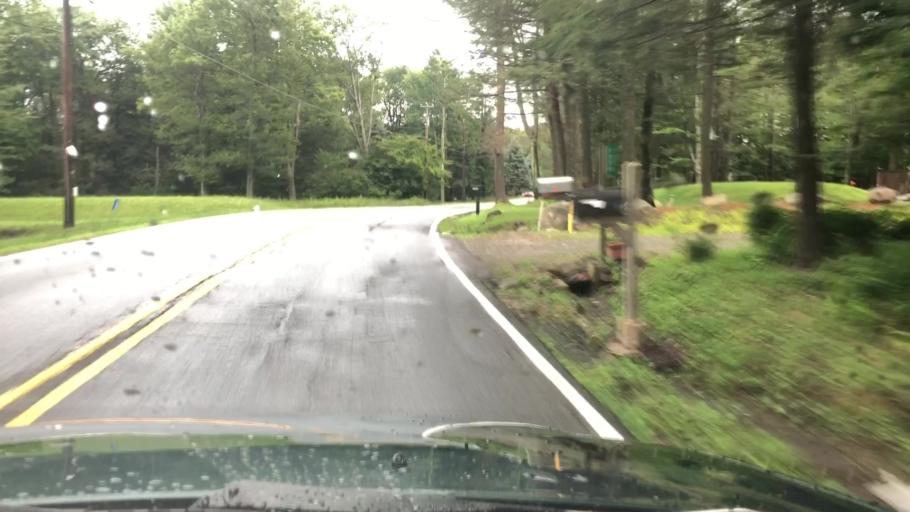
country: US
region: Pennsylvania
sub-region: Monroe County
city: Mountainhome
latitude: 41.2878
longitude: -75.2391
